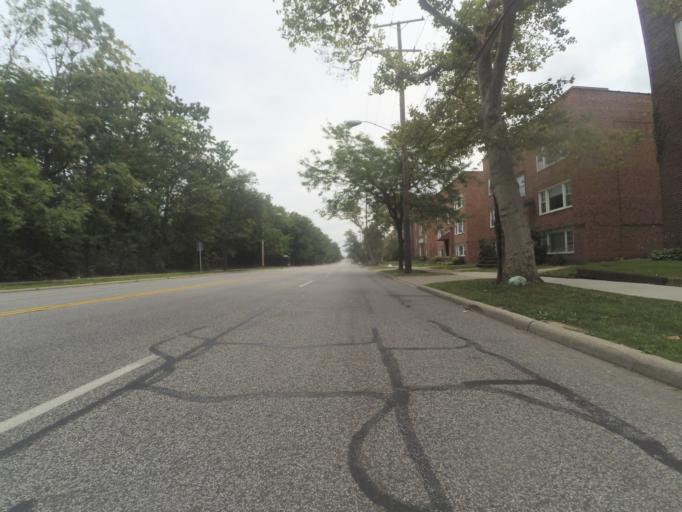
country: US
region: Ohio
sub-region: Cuyahoga County
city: East Cleveland
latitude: 41.5097
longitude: -81.5851
